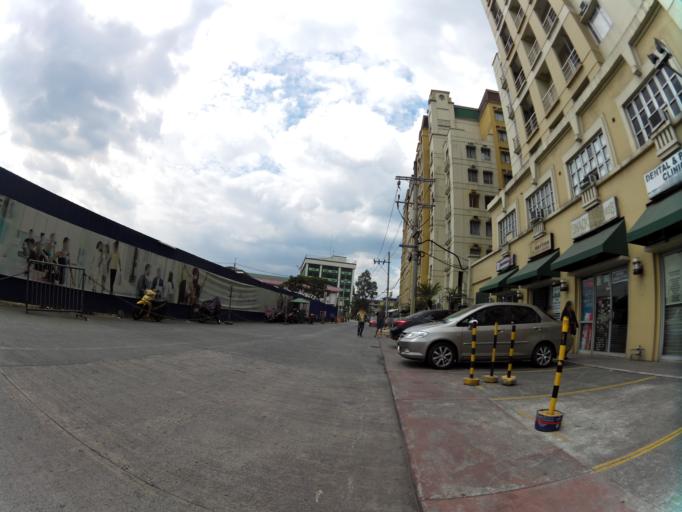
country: PH
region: Metro Manila
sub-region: Marikina
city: Calumpang
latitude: 14.6363
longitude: 121.1002
